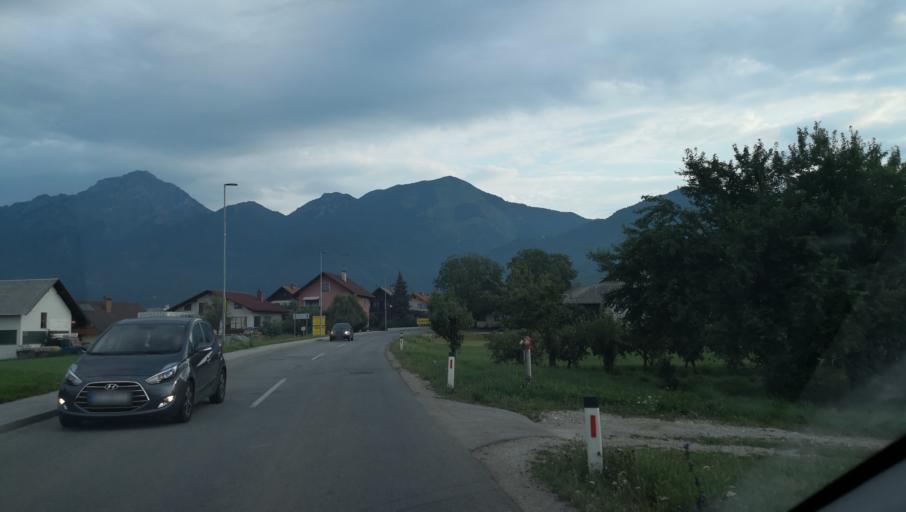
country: SI
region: Preddvor
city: Preddvor
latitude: 46.2789
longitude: 14.4217
